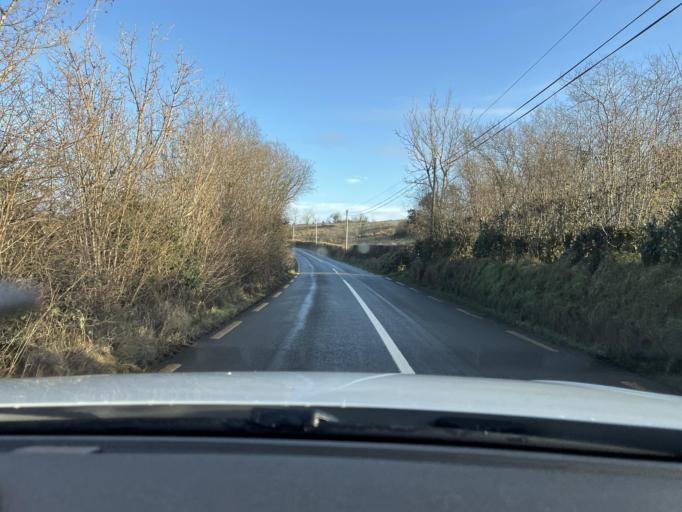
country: IE
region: Connaught
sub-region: County Leitrim
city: Manorhamilton
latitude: 54.1711
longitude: -8.1235
